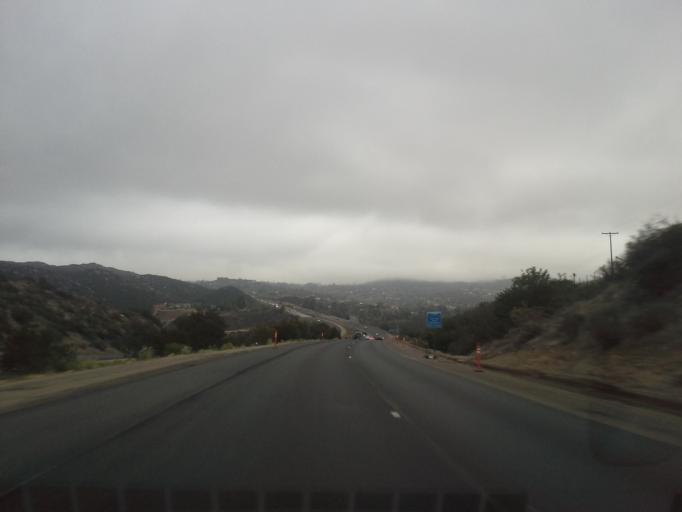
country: US
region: California
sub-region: San Diego County
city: Harbison Canyon
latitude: 32.8545
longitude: -116.8121
